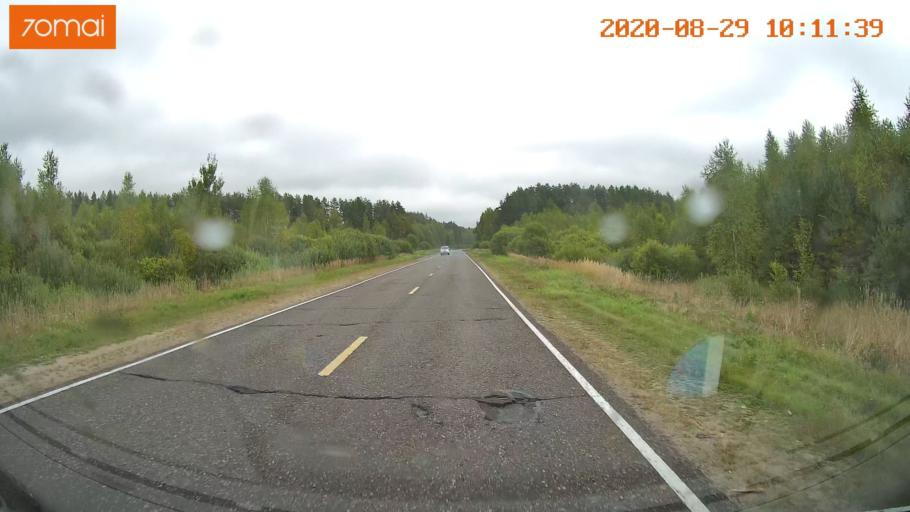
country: RU
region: Ivanovo
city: Kuznechikha
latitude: 57.3752
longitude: 42.6889
